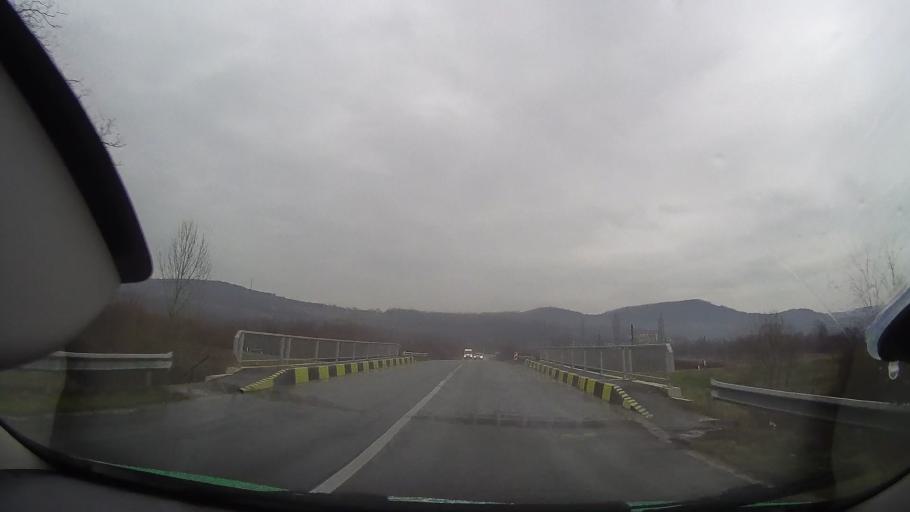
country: RO
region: Bihor
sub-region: Comuna Sambata
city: Sambata
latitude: 46.7928
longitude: 22.2037
